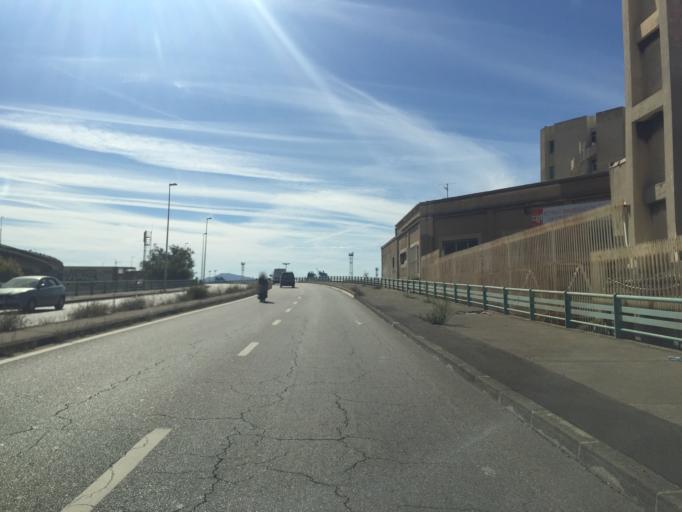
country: FR
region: Provence-Alpes-Cote d'Azur
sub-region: Departement des Bouches-du-Rhone
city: Marseille 03
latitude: 43.3197
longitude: 5.3627
